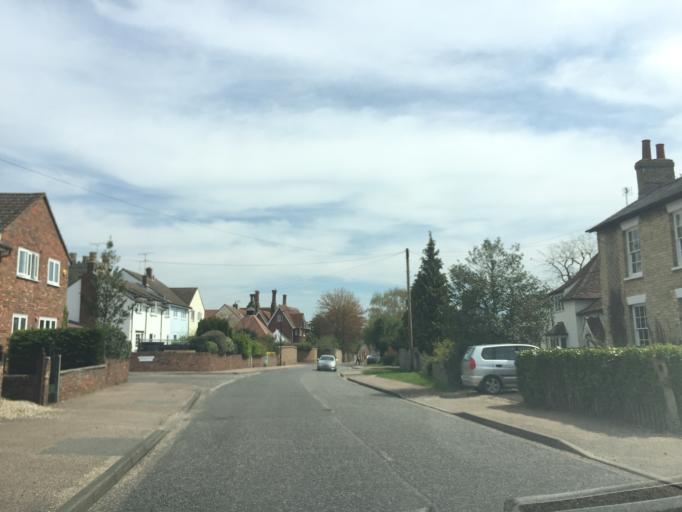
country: GB
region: England
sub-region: Essex
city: Saffron Walden
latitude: 51.9839
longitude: 0.2105
